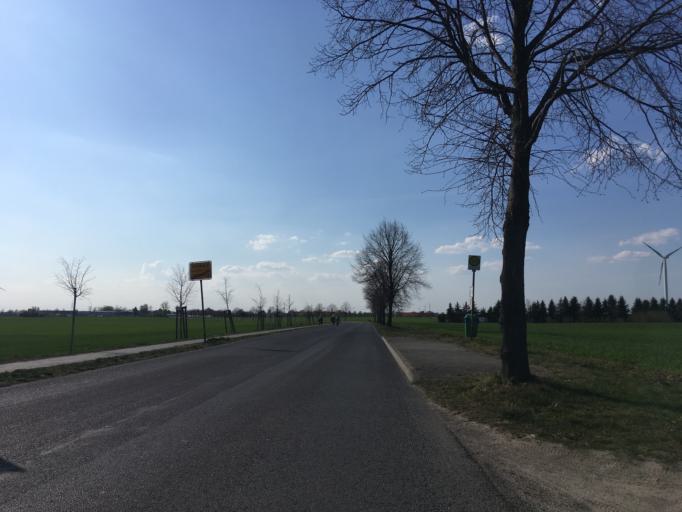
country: DE
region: Berlin
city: Falkenberg
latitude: 52.6030
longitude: 13.5456
